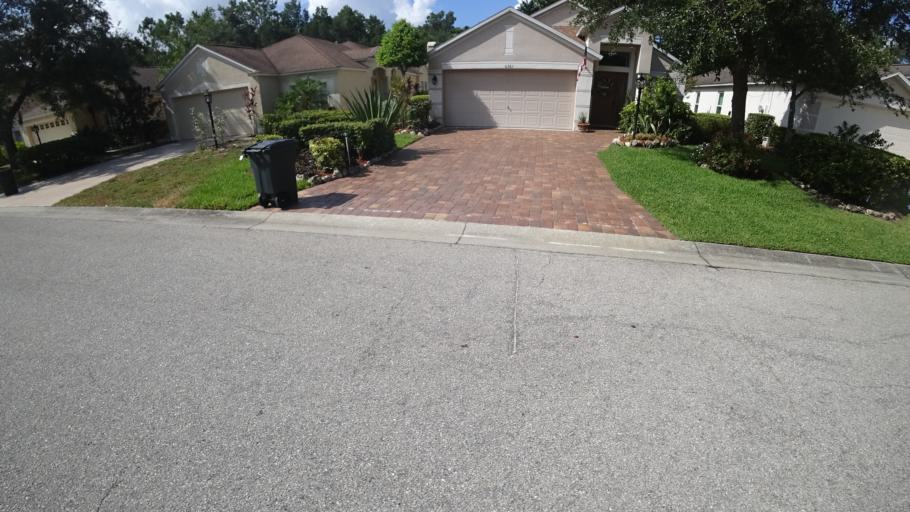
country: US
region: Florida
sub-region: Sarasota County
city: The Meadows
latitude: 27.4286
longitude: -82.4228
